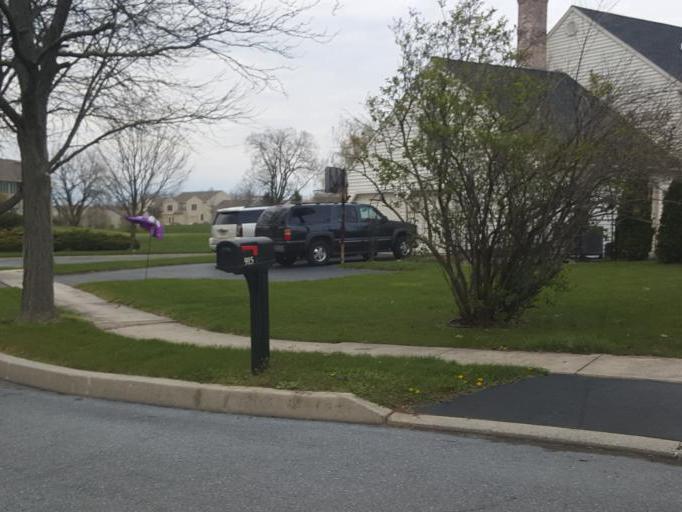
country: US
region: Pennsylvania
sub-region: Dauphin County
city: Hummelstown
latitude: 40.2424
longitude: -76.7143
